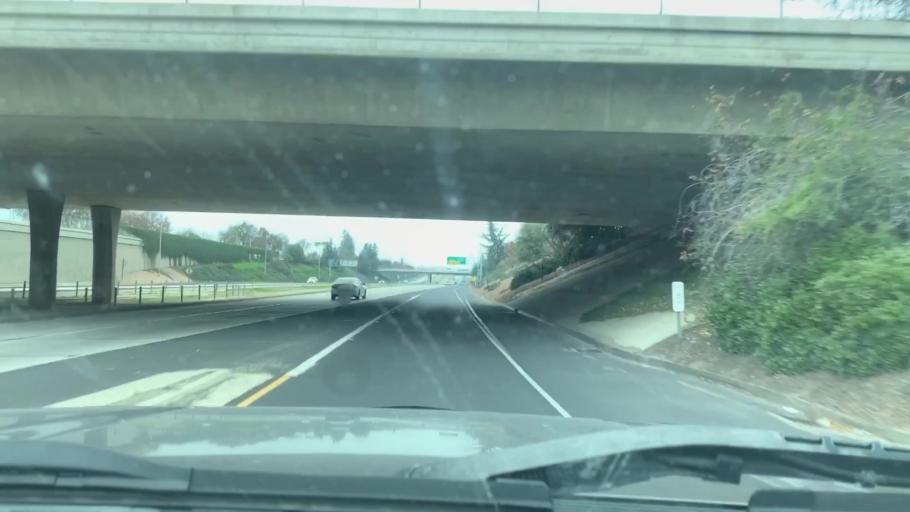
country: US
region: California
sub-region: Tulare County
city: Visalia
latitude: 36.3276
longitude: -119.3360
